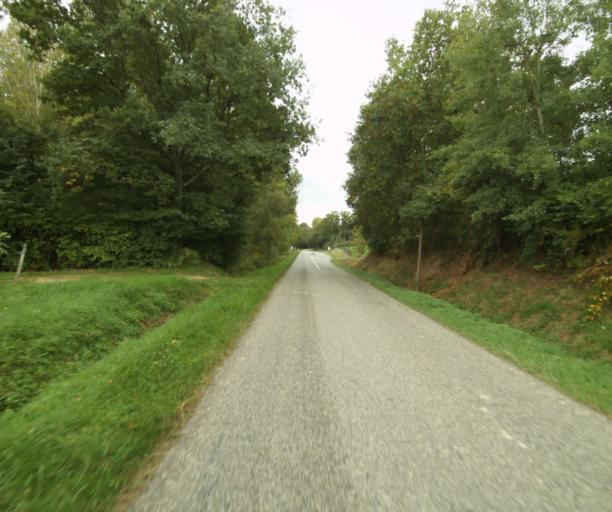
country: FR
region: Midi-Pyrenees
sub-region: Departement du Gers
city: Eauze
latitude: 43.9006
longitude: 0.0995
